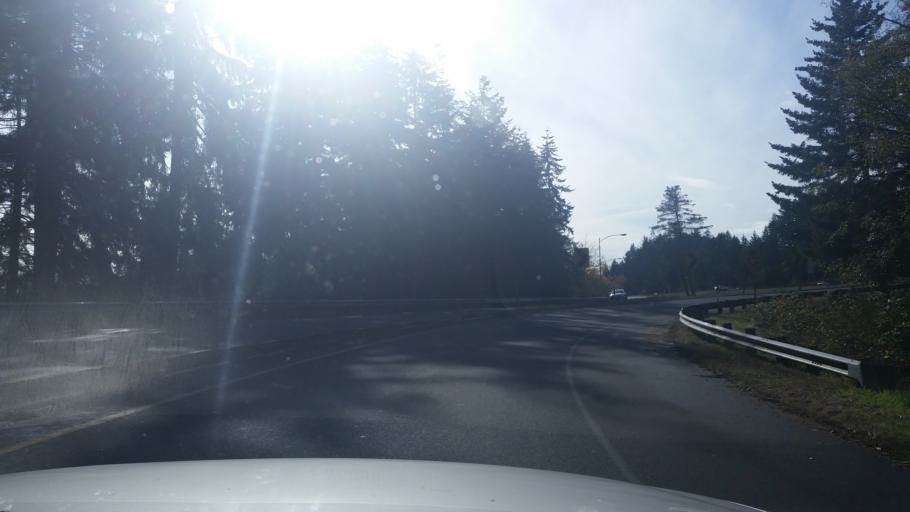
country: US
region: Washington
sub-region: Snohomish County
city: Mountlake Terrace
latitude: 47.7765
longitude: -122.3162
